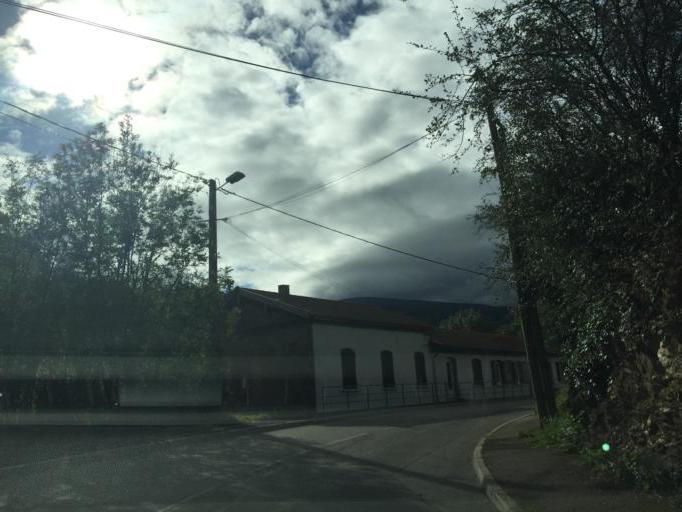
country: FR
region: Rhone-Alpes
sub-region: Departement de la Loire
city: Saint-Paul-en-Jarez
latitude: 45.4532
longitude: 4.5822
